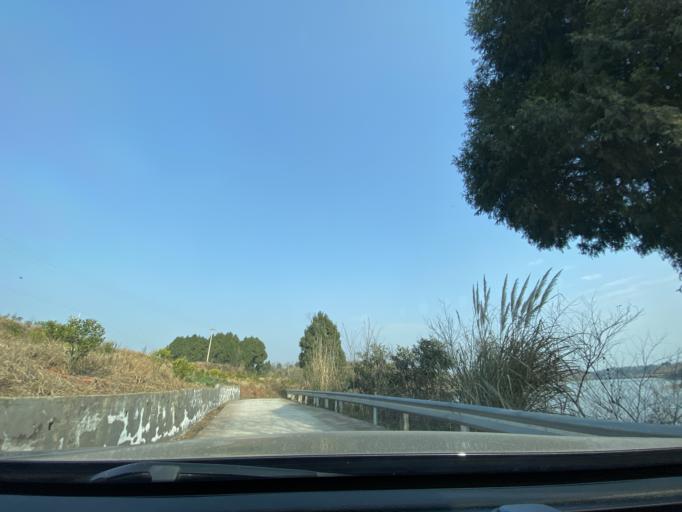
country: CN
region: Sichuan
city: Wenlin
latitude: 30.2508
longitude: 104.2525
